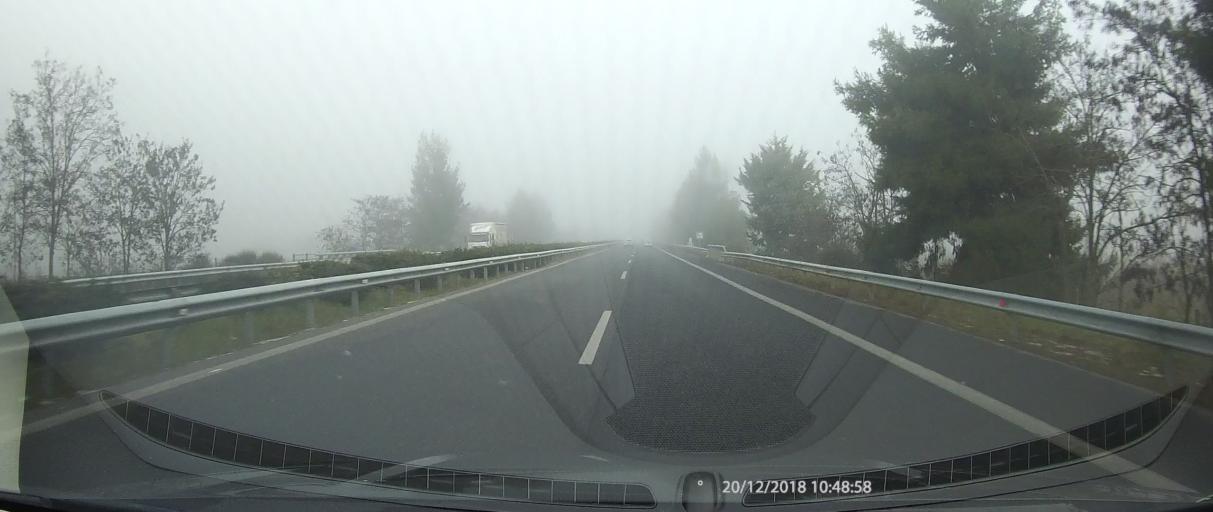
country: GR
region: Peloponnese
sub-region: Nomos Arkadias
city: Tripoli
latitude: 37.5283
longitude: 22.4106
